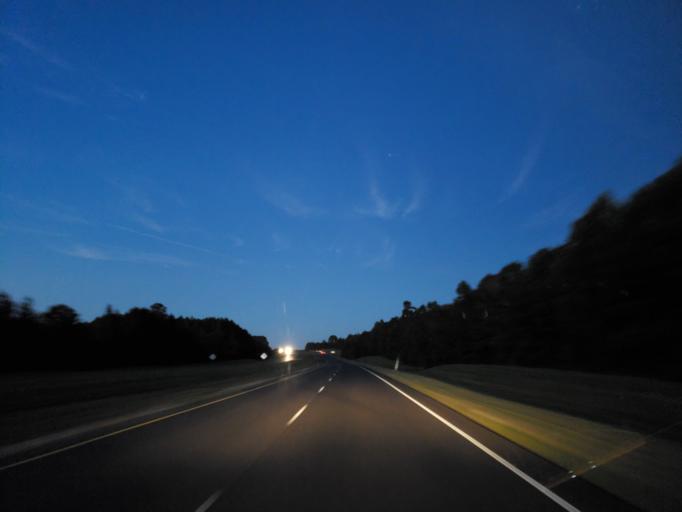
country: US
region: Mississippi
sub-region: Clarke County
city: Quitman
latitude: 32.0006
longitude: -88.6939
